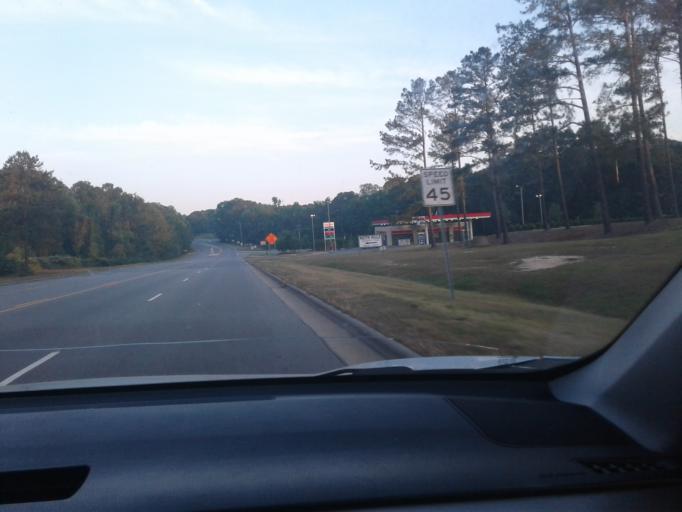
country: US
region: North Carolina
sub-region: Harnett County
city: Buies Creek
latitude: 35.4061
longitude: -78.7441
